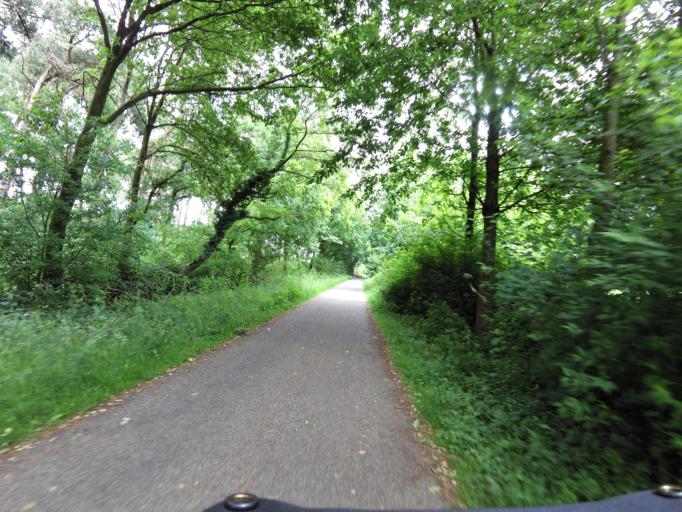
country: NL
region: North Brabant
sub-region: Gemeente Baarle-Nassau
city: Baarle-Nassau
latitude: 51.4542
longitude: 4.9293
